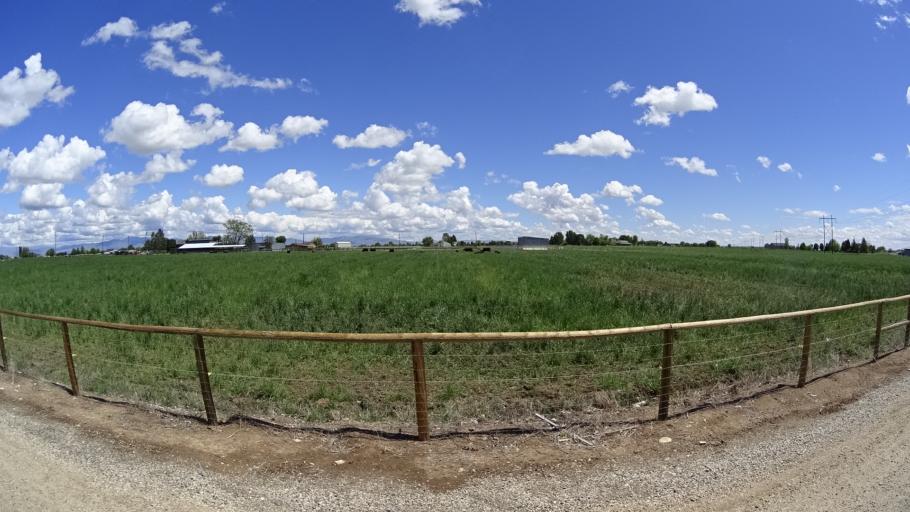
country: US
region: Idaho
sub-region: Ada County
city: Meridian
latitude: 43.5595
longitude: -116.4338
